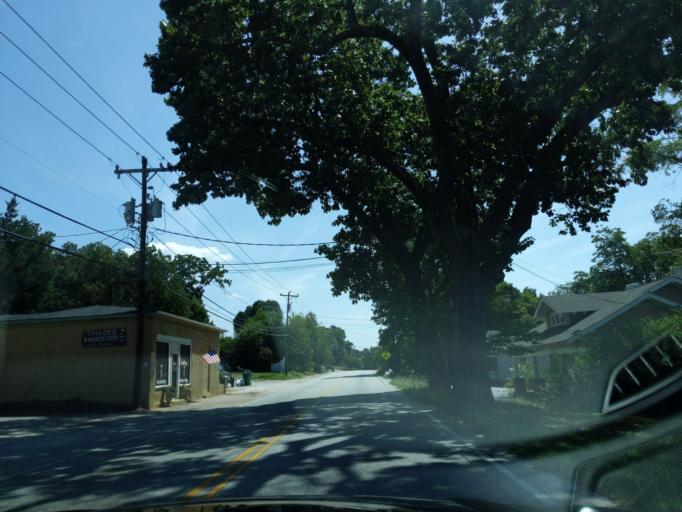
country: US
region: South Carolina
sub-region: Greenville County
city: Taylors
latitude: 34.9201
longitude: -82.3000
